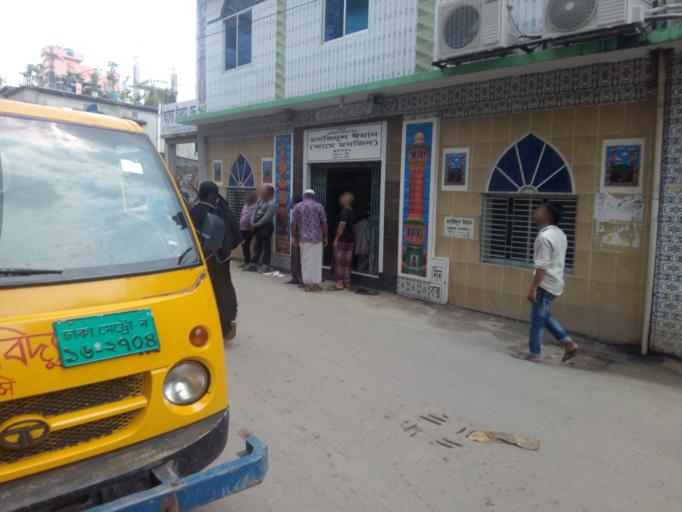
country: BD
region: Dhaka
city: Azimpur
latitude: 23.7174
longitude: 90.3724
